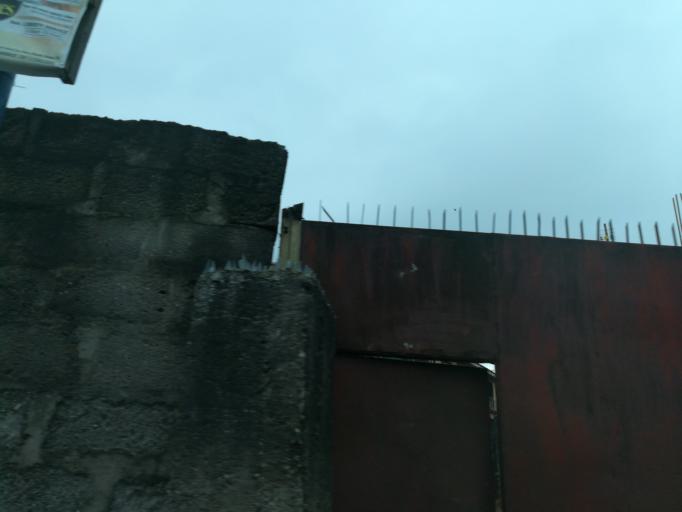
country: NG
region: Rivers
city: Port Harcourt
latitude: 4.8168
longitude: 7.0190
